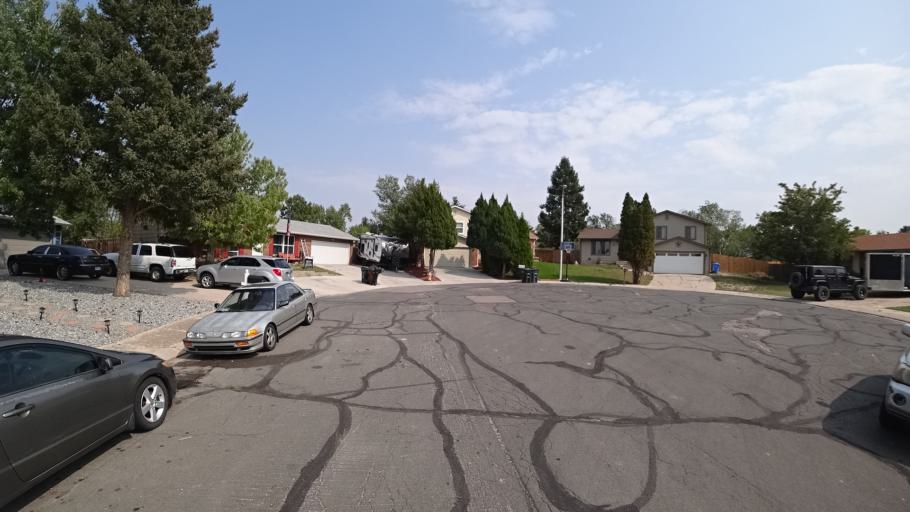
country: US
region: Colorado
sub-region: El Paso County
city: Stratmoor
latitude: 38.8278
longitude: -104.7549
